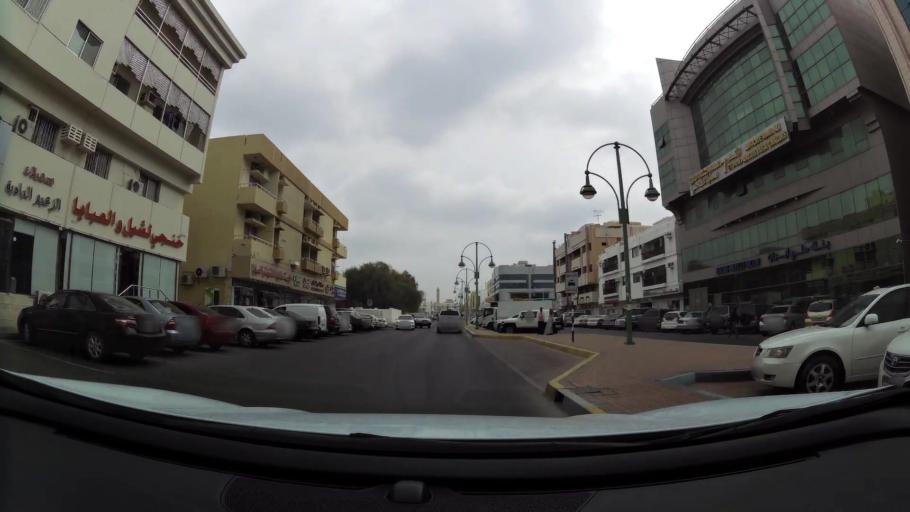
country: AE
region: Abu Dhabi
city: Al Ain
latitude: 24.2217
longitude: 55.7599
